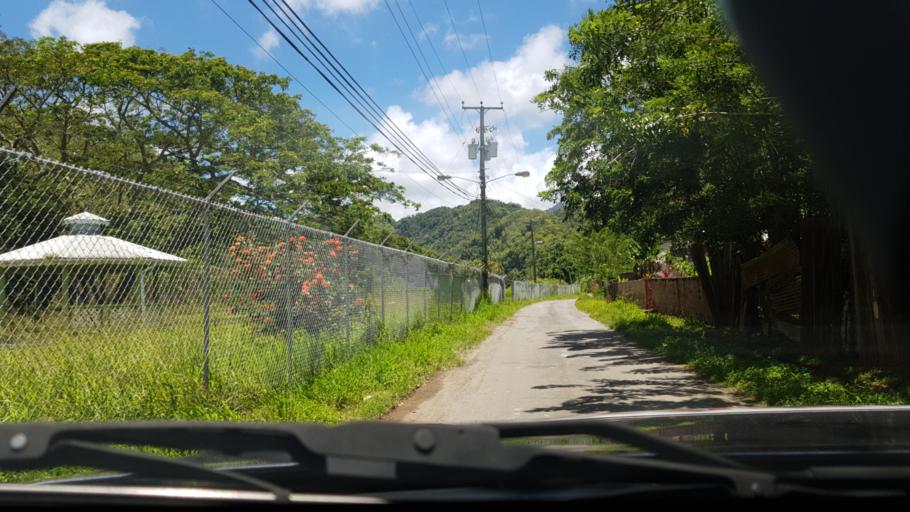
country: LC
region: Anse-la-Raye
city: Canaries
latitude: 13.9025
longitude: -61.0640
